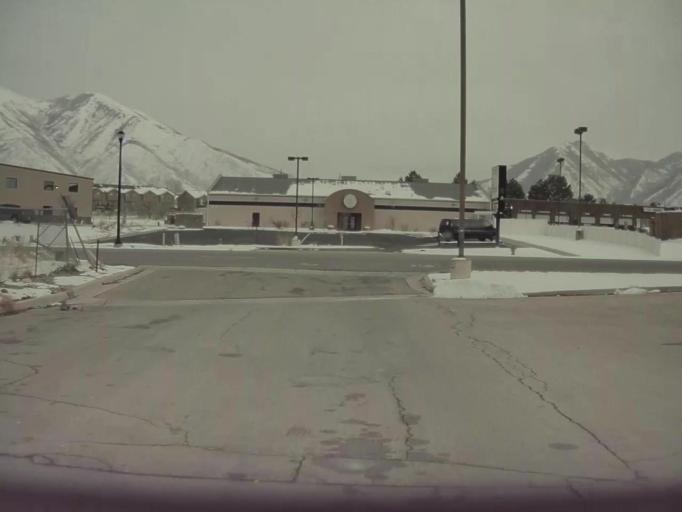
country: US
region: Utah
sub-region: Utah County
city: Spanish Fork
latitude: 40.1221
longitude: -111.6385
